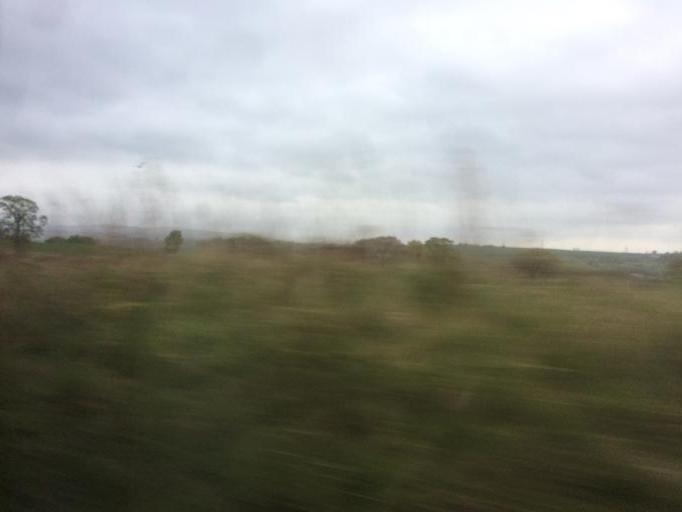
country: GB
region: Scotland
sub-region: Falkirk
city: Bonnybridge
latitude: 55.9840
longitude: -3.9166
